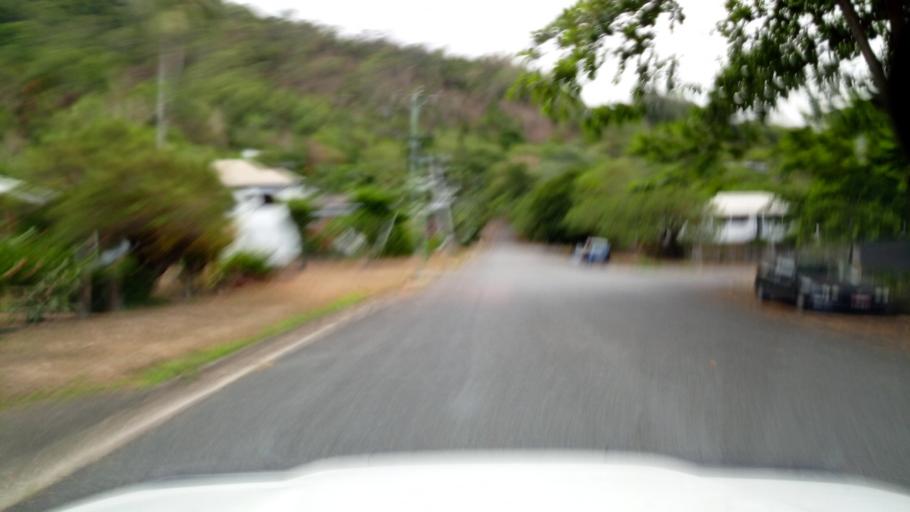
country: AU
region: Queensland
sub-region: Cairns
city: Redlynch
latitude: -16.8765
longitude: 145.7318
